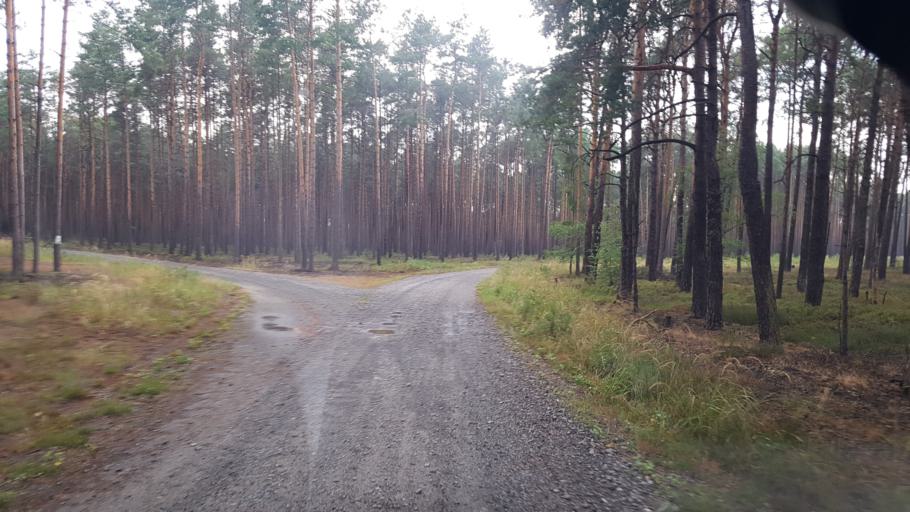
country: DE
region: Brandenburg
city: Sallgast
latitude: 51.6319
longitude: 13.7956
